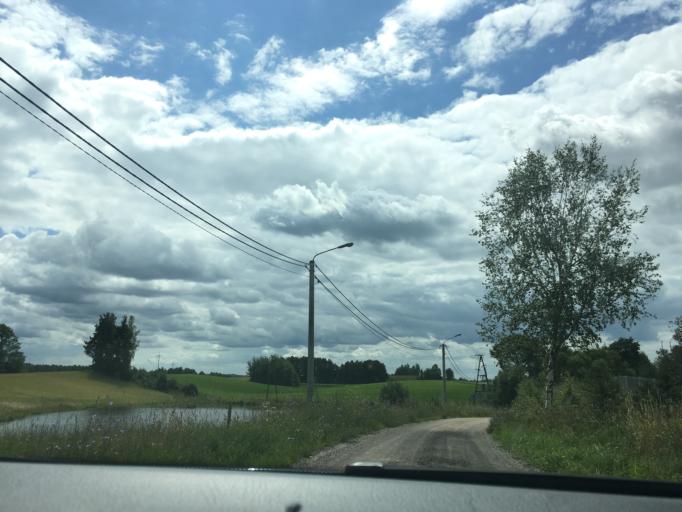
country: PL
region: Podlasie
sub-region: Powiat sejnenski
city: Krasnopol
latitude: 54.0936
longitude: 23.2696
